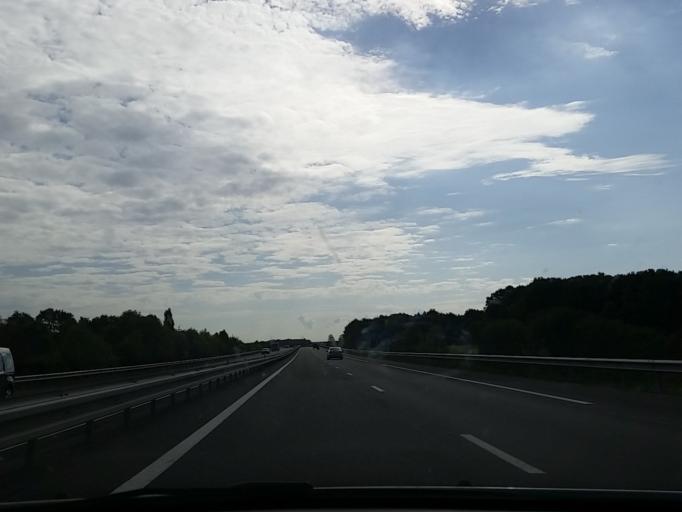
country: FR
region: Centre
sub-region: Departement du Loir-et-Cher
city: Chatres-sur-Cher
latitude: 47.2958
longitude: 1.9029
